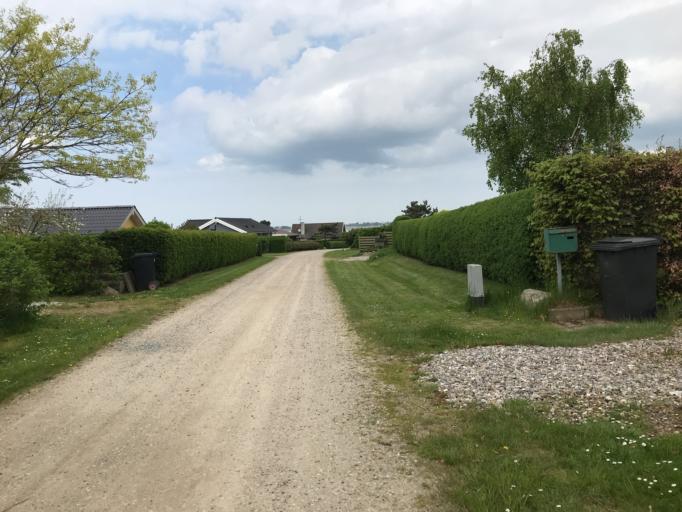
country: DK
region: South Denmark
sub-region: Assens Kommune
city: Assens
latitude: 55.3320
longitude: 9.8803
